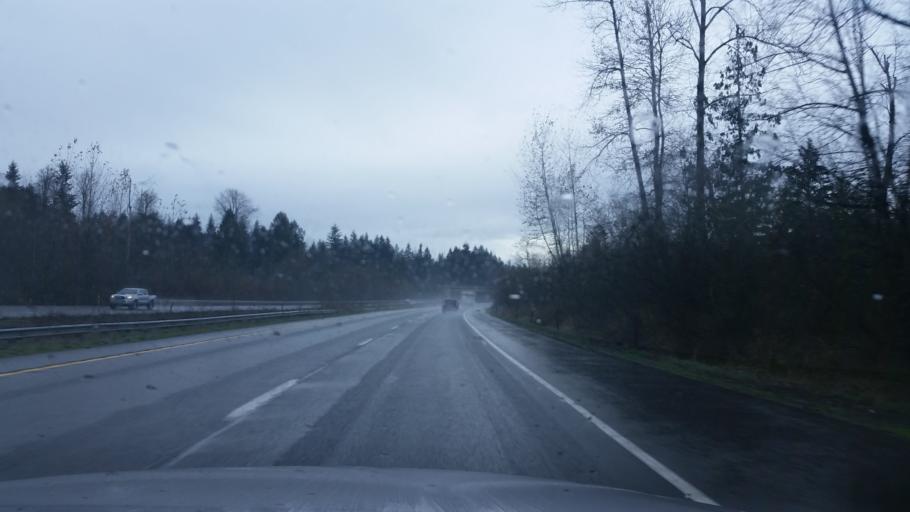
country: US
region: Washington
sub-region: King County
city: Hobart
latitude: 47.4250
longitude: -121.9934
